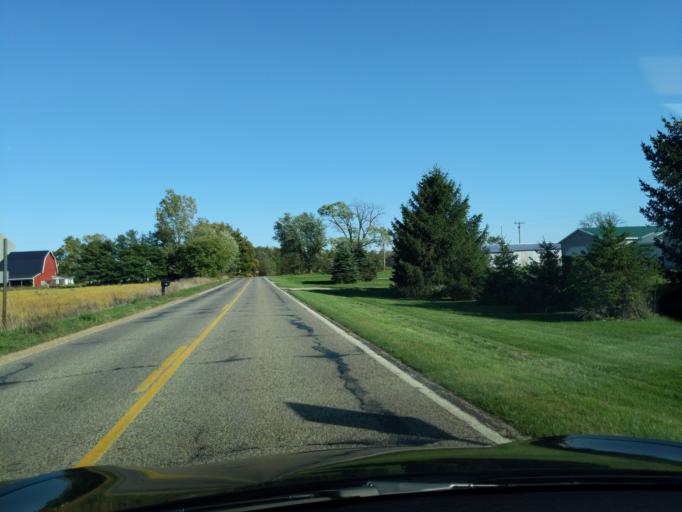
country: US
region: Michigan
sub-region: Clinton County
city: Saint Johns
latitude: 42.9289
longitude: -84.4811
